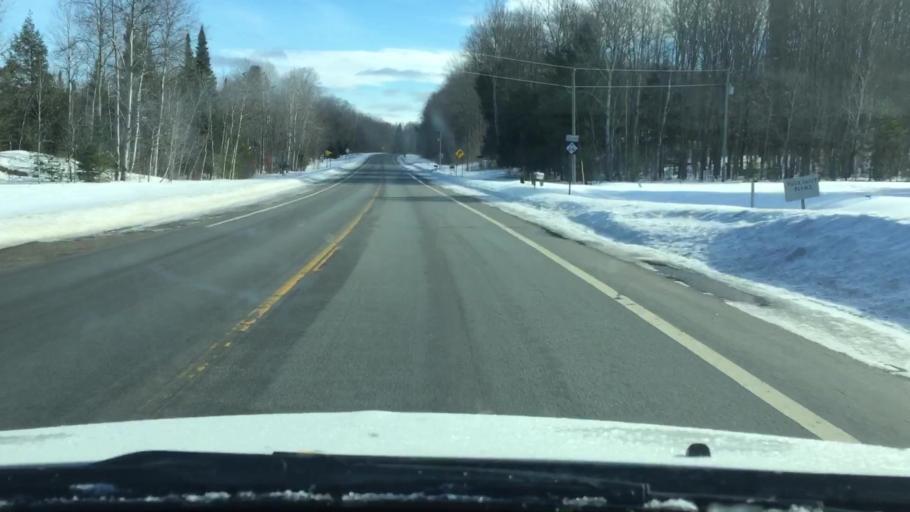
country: US
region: Michigan
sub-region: Antrim County
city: Mancelona
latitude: 44.9892
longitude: -85.0598
